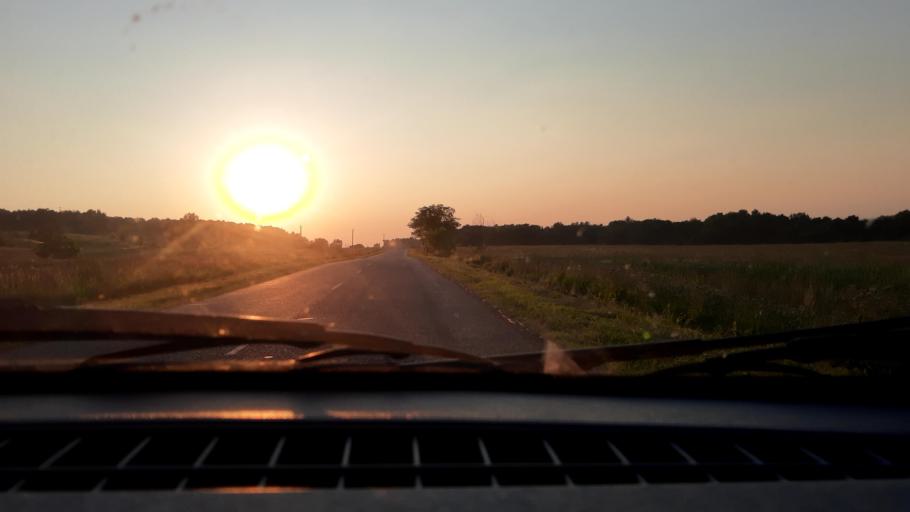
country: RU
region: Bashkortostan
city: Blagoveshchensk
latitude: 54.9366
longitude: 55.8942
